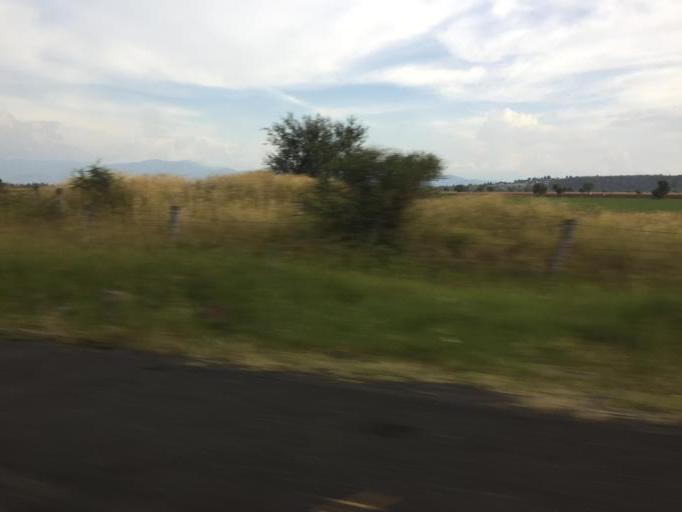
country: MX
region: Michoacan
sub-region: Alvaro Obregon
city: Lazaro Cardenas (La Purisima)
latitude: 19.8913
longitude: -101.0277
